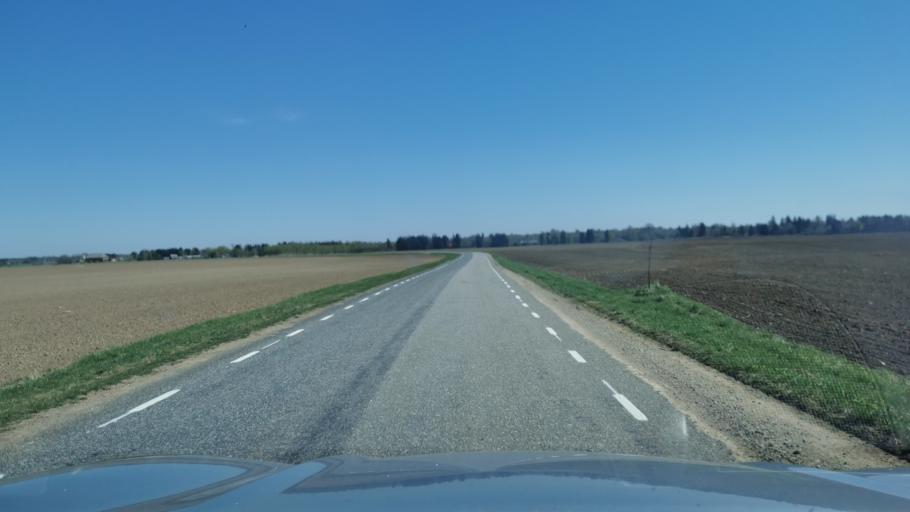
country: EE
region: Laeaene-Virumaa
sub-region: Vinni vald
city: Vinni
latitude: 59.0863
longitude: 26.6066
